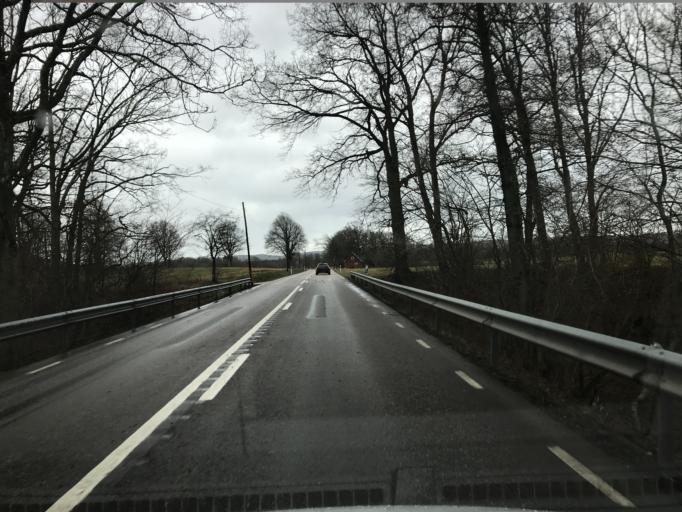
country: SE
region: Skane
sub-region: Klippans Kommun
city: Klippan
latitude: 56.1089
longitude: 13.1778
